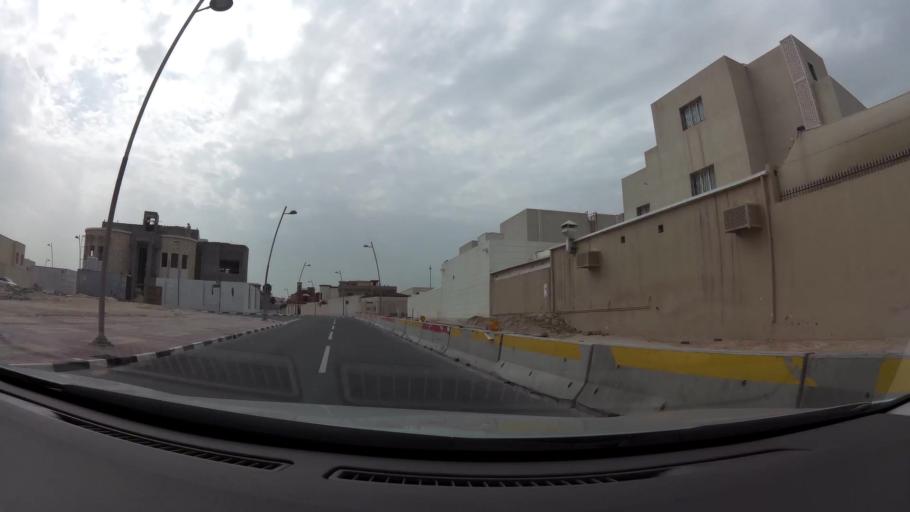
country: QA
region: Baladiyat ad Dawhah
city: Doha
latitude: 25.3439
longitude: 51.4877
